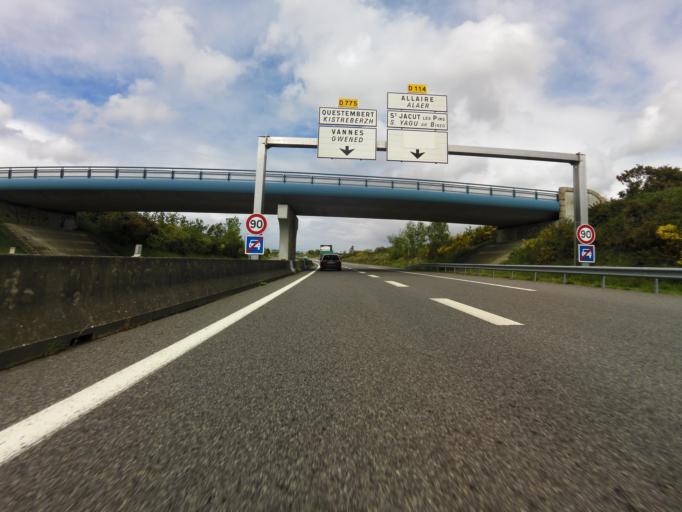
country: FR
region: Brittany
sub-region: Departement du Morbihan
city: Allaire
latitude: 47.6292
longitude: -2.1699
